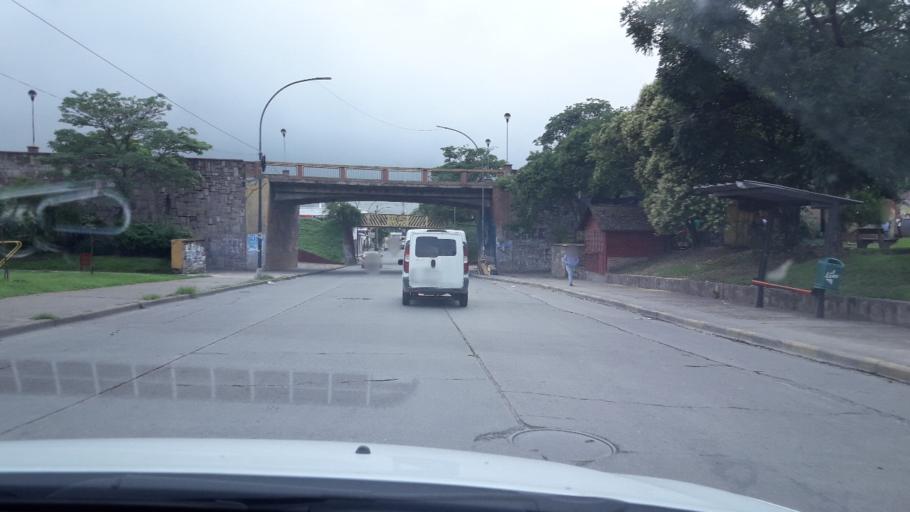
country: AR
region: Jujuy
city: San Salvador de Jujuy
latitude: -24.1921
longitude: -65.2938
